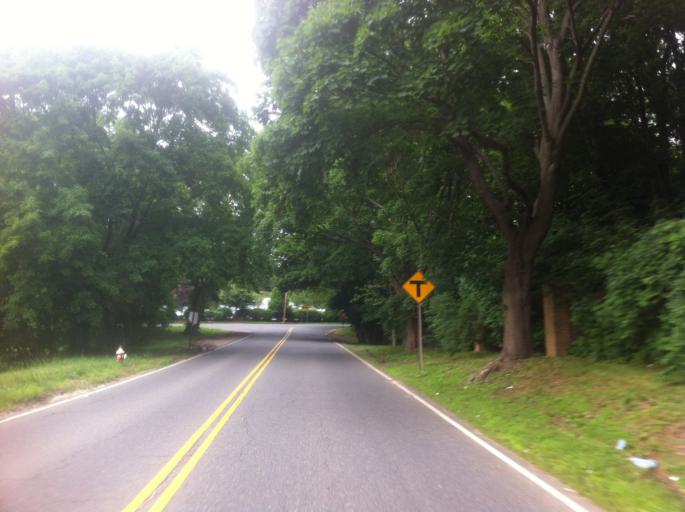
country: US
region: New York
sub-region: Nassau County
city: Old Brookville
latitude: 40.8327
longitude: -73.5920
